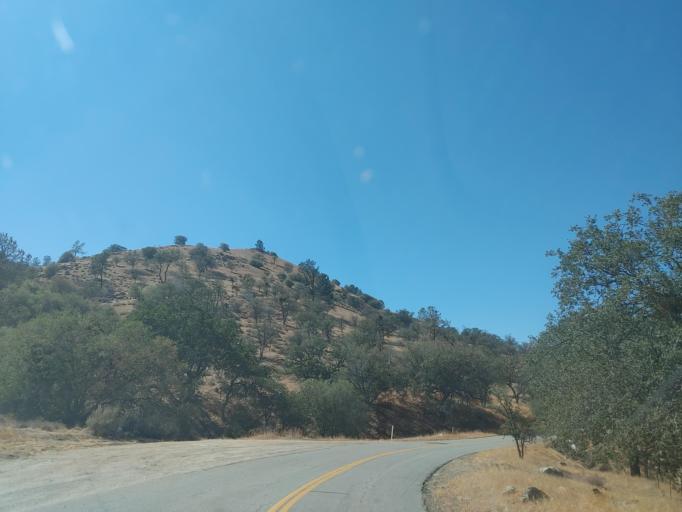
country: US
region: California
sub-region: Kern County
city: Golden Hills
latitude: 35.1861
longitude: -118.5171
